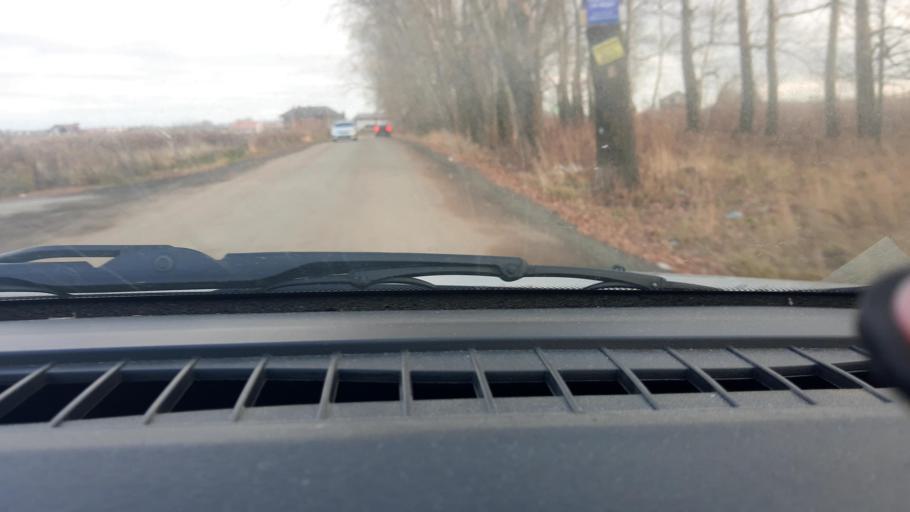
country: RU
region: Nizjnij Novgorod
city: Afonino
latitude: 56.2697
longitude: 44.0477
